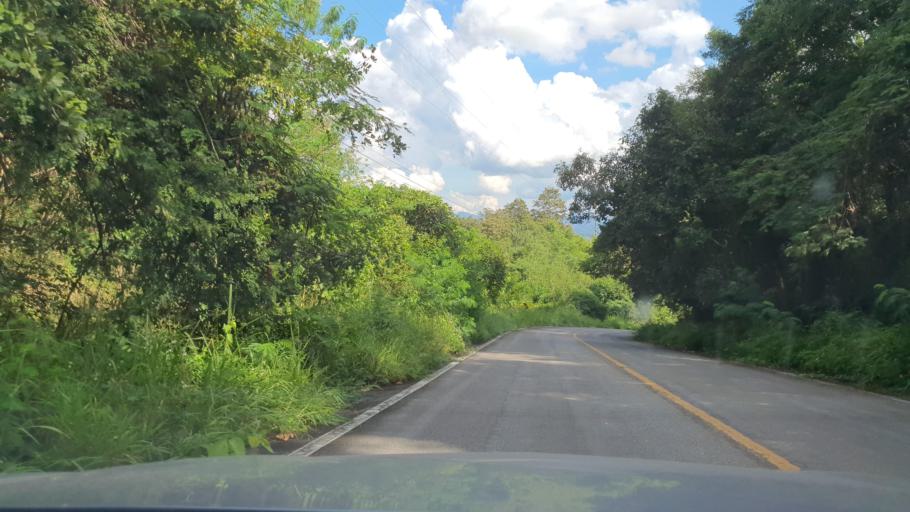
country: TH
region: Chiang Rai
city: Wiang Pa Pao
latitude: 19.3318
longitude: 99.4611
